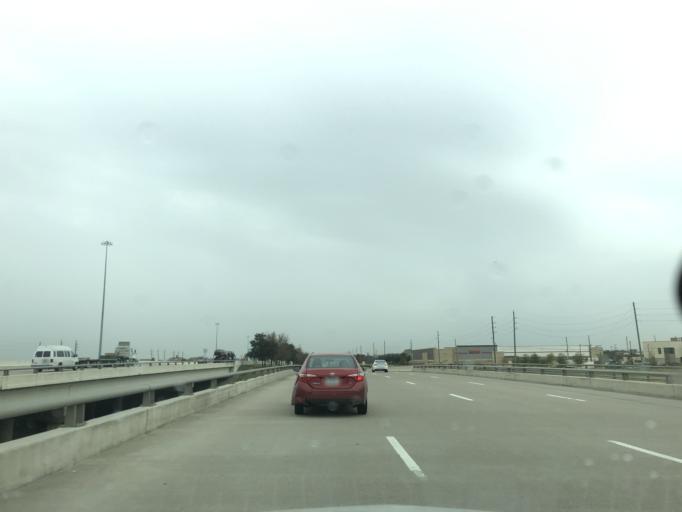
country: US
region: Texas
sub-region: Fort Bend County
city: Sugar Land
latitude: 29.5869
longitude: -95.6393
